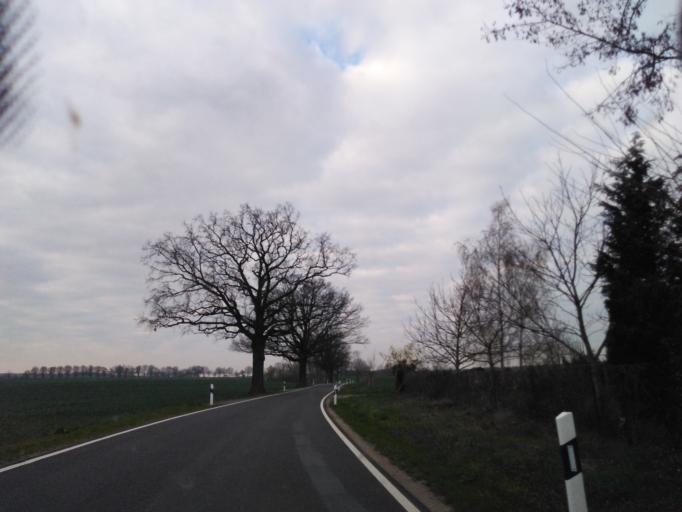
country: DE
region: Brandenburg
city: Buckow
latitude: 52.6356
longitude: 14.0728
